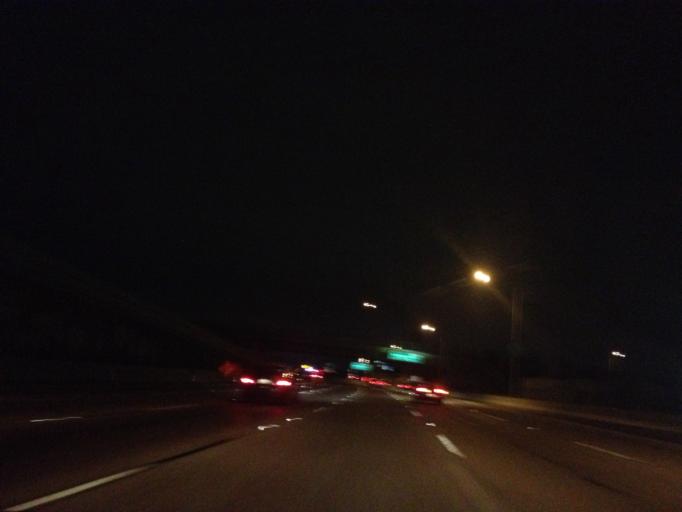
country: US
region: California
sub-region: Orange County
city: Placentia
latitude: 33.8560
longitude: -117.8754
